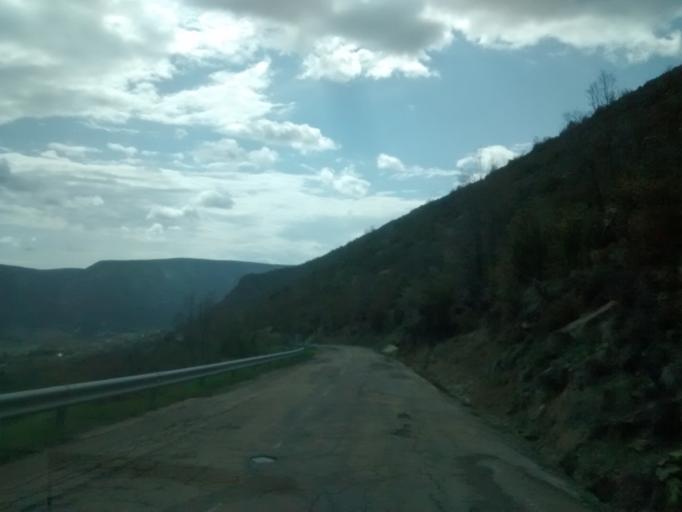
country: ES
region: Aragon
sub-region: Provincia de Huesca
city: Arguis
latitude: 42.3272
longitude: -0.4182
